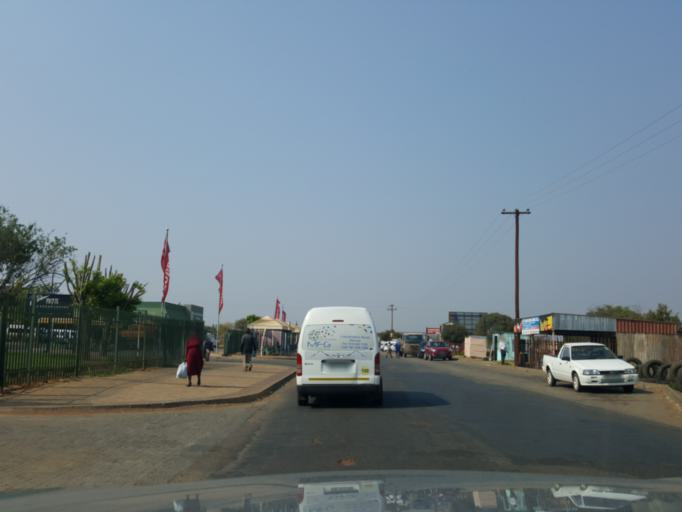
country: ZA
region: North-West
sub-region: Ngaka Modiri Molema District Municipality
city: Zeerust
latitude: -25.4930
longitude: 25.9842
